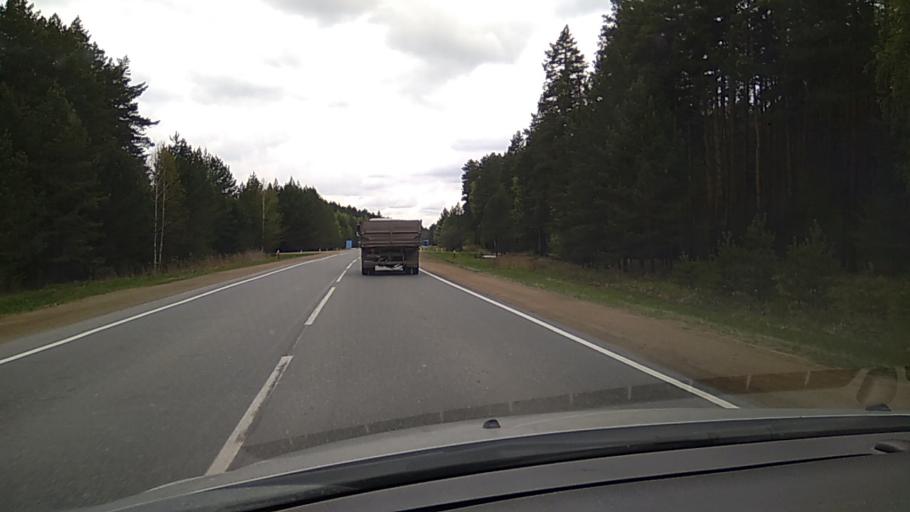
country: RU
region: Kurgan
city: Kataysk
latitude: 56.3007
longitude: 62.3731
